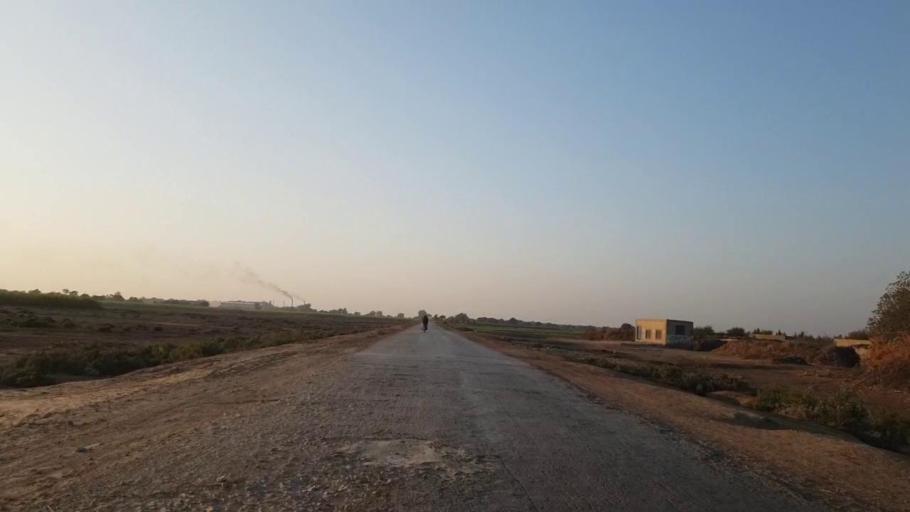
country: PK
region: Sindh
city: Chambar
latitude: 25.2432
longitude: 68.6876
